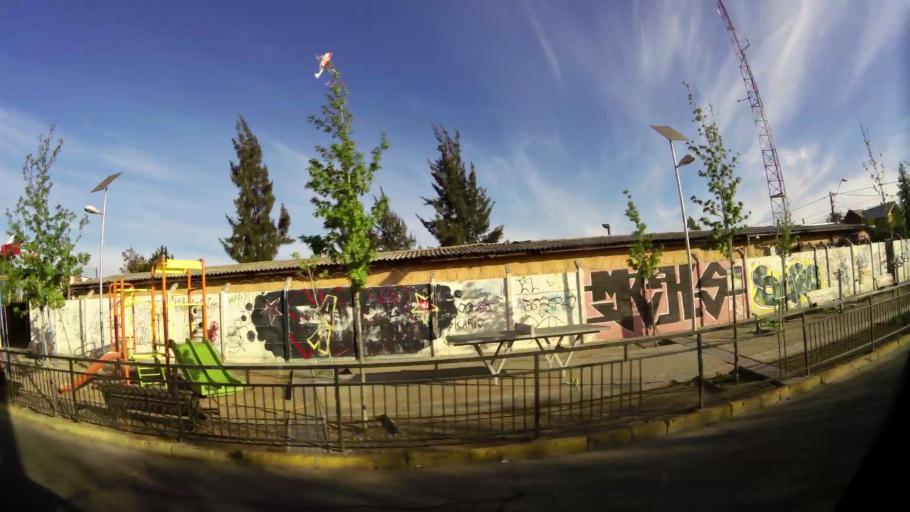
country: CL
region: Santiago Metropolitan
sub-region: Provincia de Santiago
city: Lo Prado
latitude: -33.4363
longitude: -70.7008
